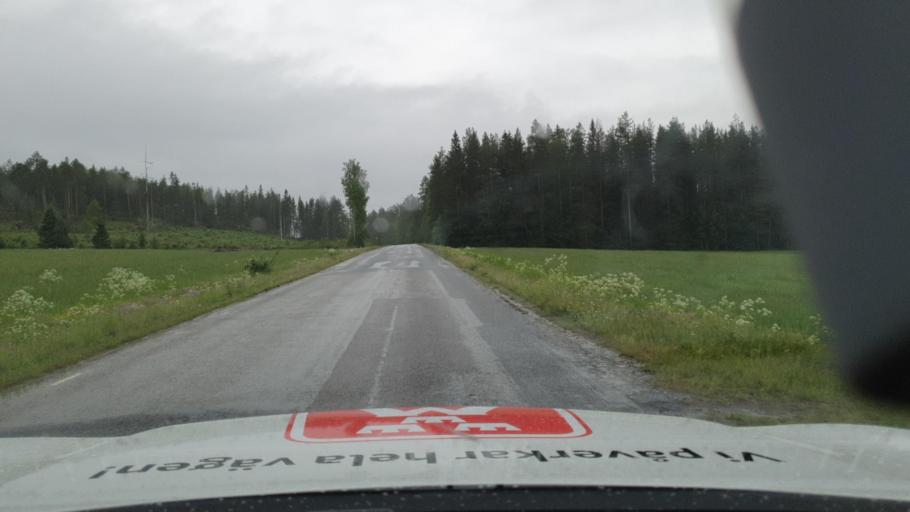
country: SE
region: Vaesterbotten
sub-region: Nordmalings Kommun
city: Nordmaling
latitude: 63.8052
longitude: 19.5038
